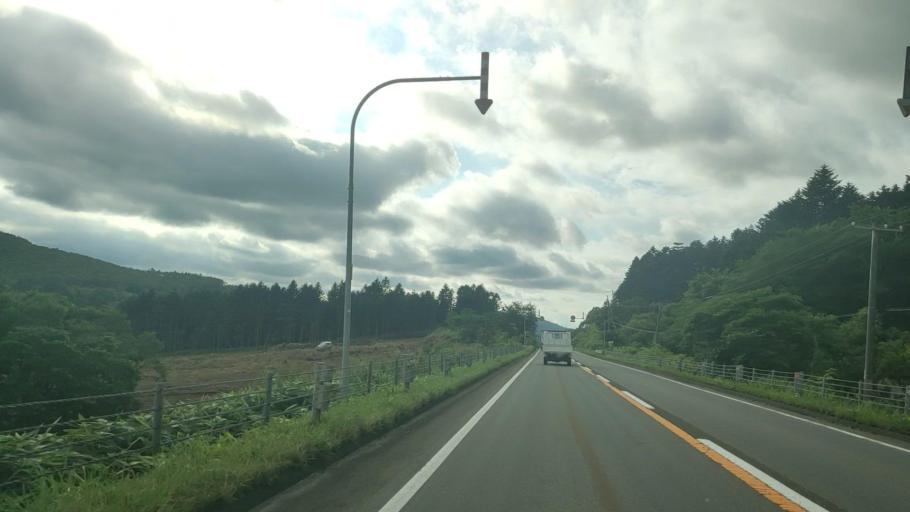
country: JP
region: Hokkaido
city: Niseko Town
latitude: 42.5968
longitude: 140.5038
